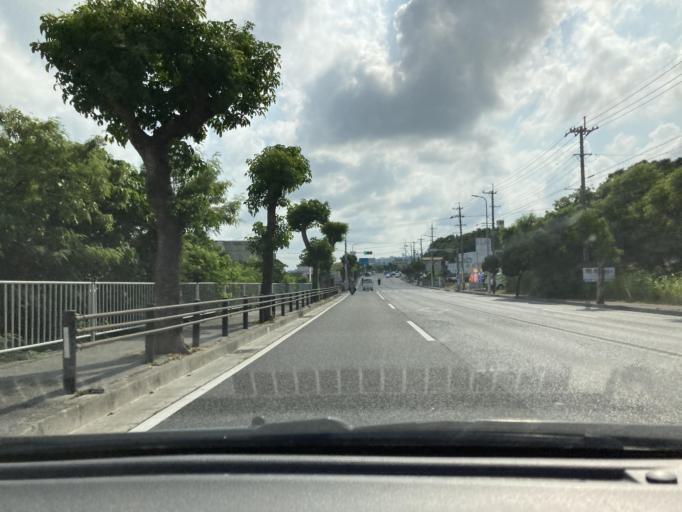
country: JP
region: Okinawa
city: Ginowan
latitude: 26.2752
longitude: 127.7986
